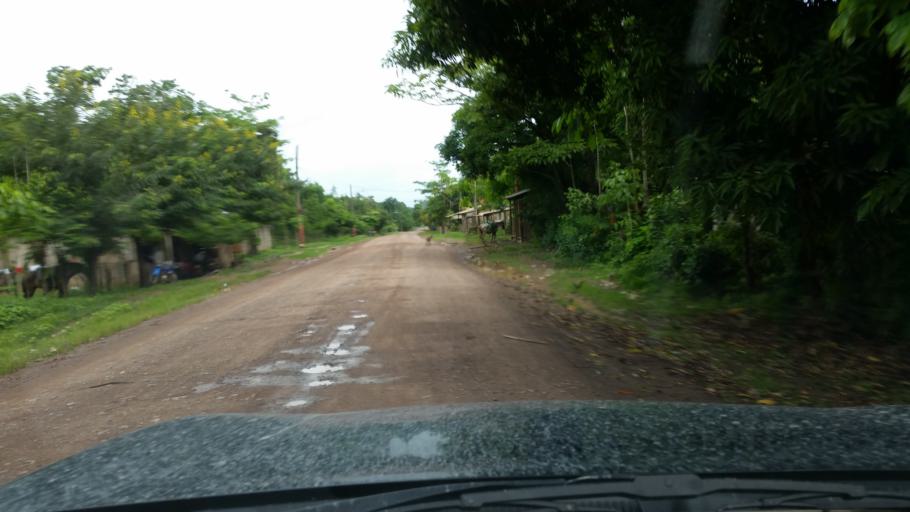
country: NI
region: Atlantico Norte (RAAN)
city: Siuna
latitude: 13.4929
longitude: -84.8447
